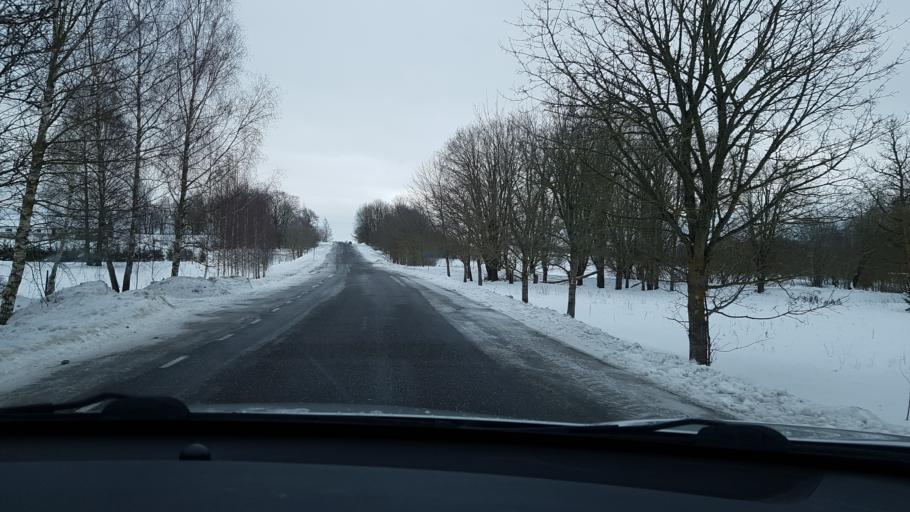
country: EE
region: Jaervamaa
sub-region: Koeru vald
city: Koeru
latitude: 58.9835
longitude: 25.9879
